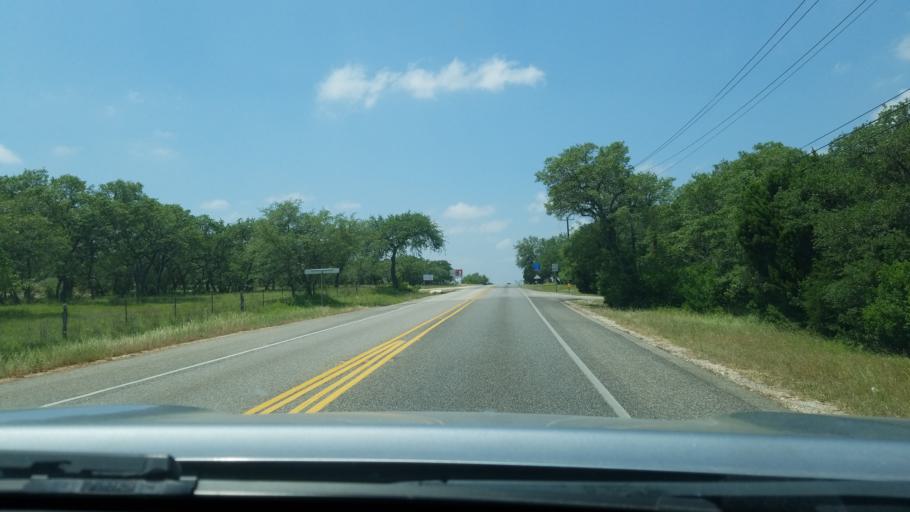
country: US
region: Texas
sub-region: Hays County
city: Woodcreek
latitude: 30.0212
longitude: -98.1543
